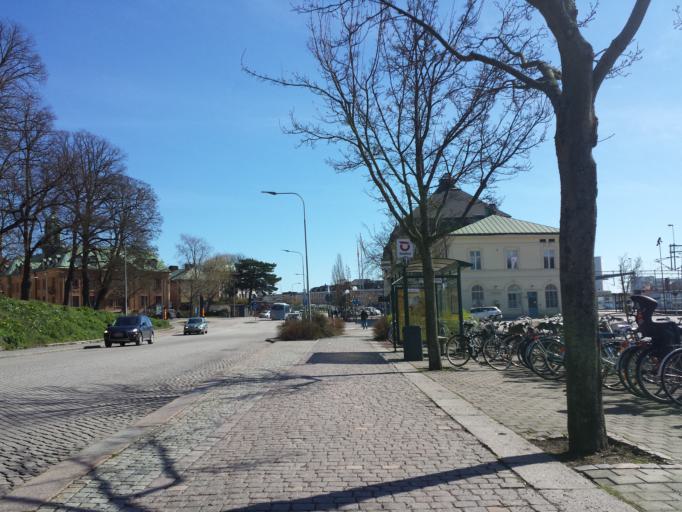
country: SE
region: Kalmar
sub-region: Kalmar Kommun
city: Kalmar
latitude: 56.6619
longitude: 16.3589
